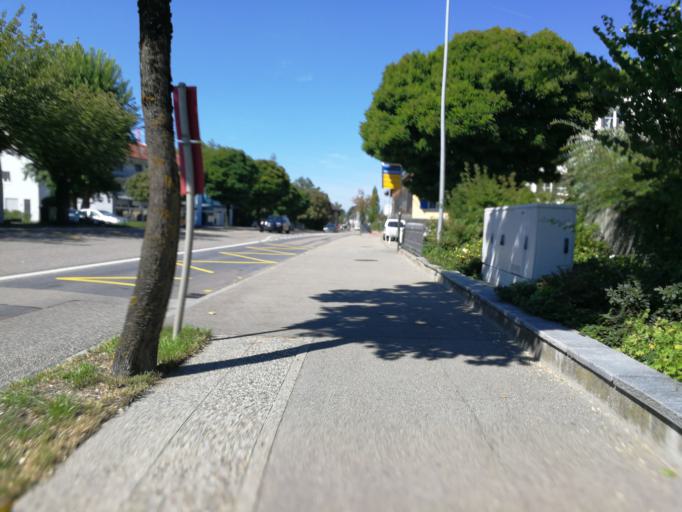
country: CH
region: Zurich
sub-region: Bezirk Pfaeffikon
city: Pfaeffikon / Irgenhausen
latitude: 47.3612
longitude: 8.7923
